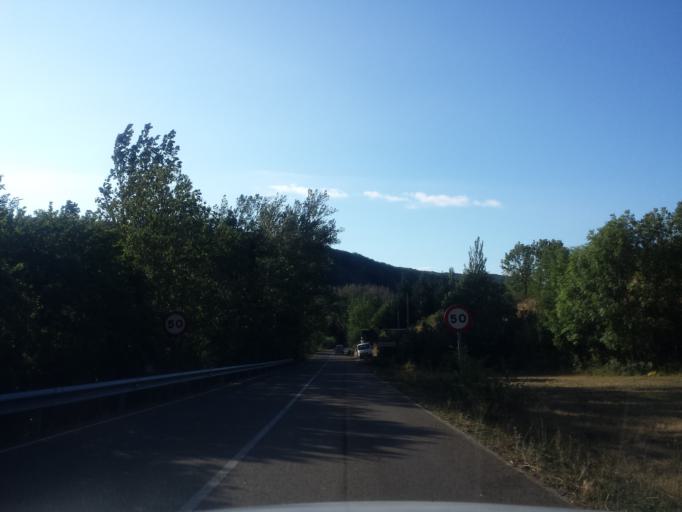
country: ES
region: Castille and Leon
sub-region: Provincia de Leon
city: Vegacervera
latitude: 42.8916
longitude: -5.5362
